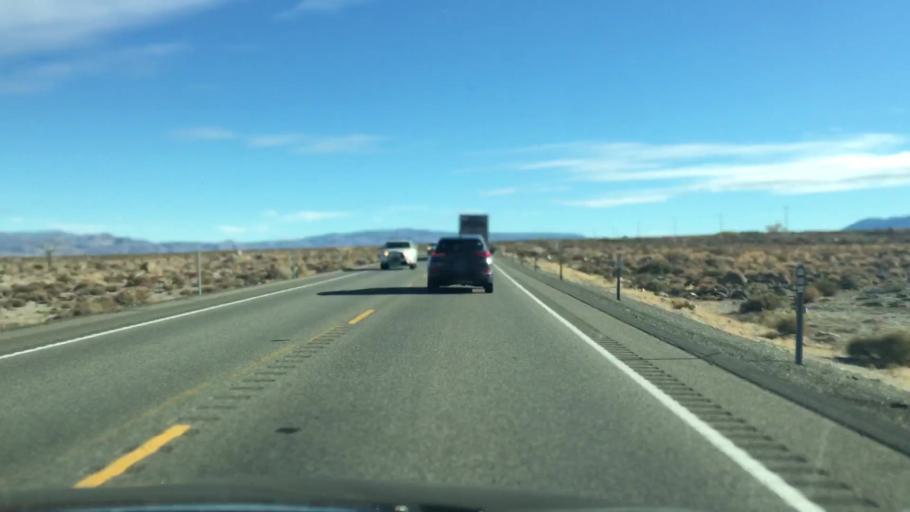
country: US
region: Nevada
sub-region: Mineral County
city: Hawthorne
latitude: 38.5729
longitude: -118.6941
